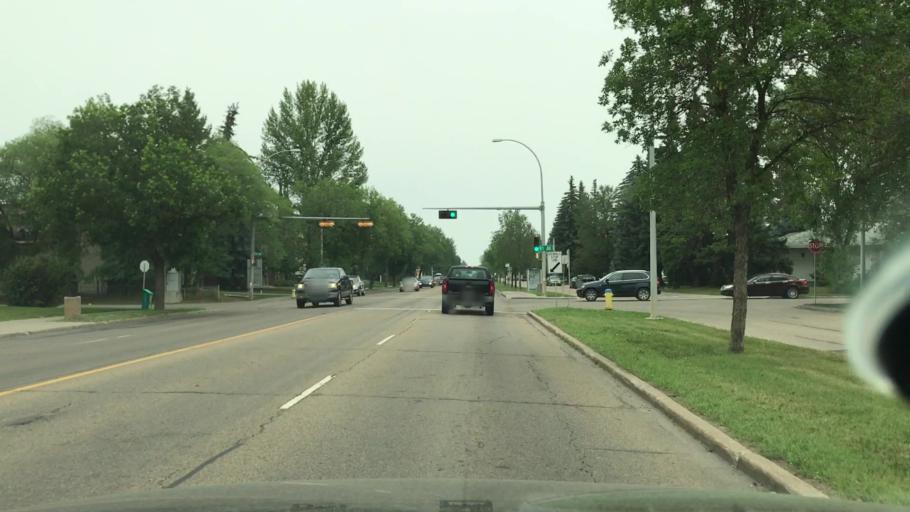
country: CA
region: Alberta
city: Edmonton
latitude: 53.5244
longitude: -113.5779
